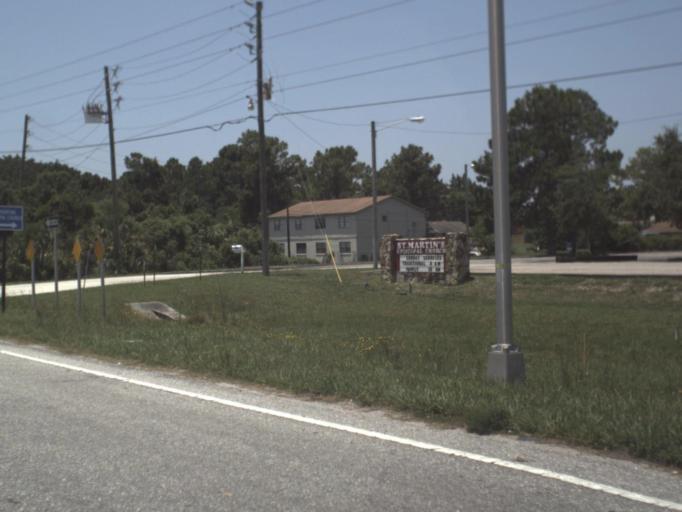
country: US
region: Florida
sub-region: Pasco County
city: Hudson
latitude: 28.3864
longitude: -82.6724
